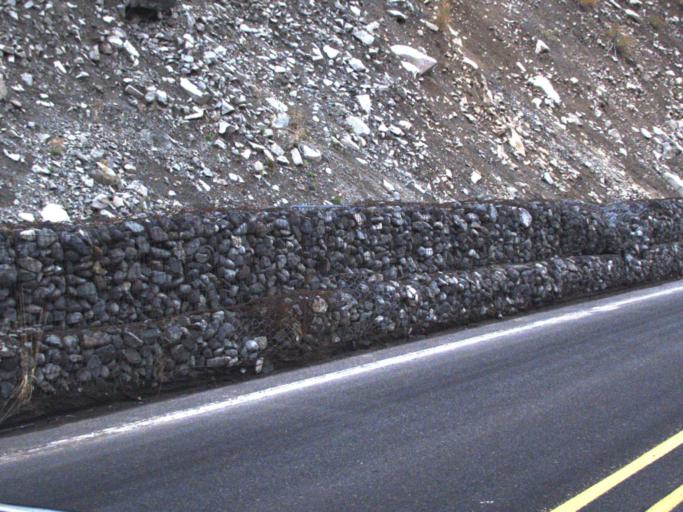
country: US
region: Washington
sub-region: Yakima County
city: Tieton
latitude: 46.6621
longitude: -121.4801
